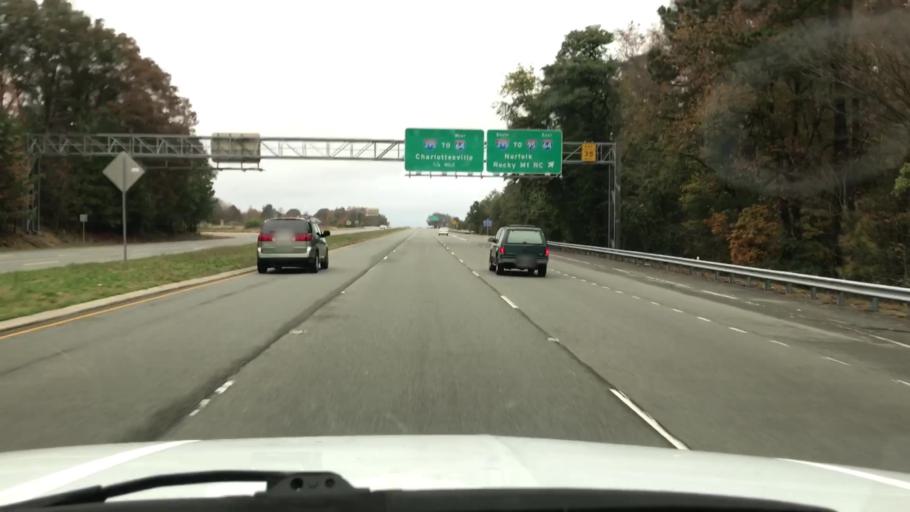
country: US
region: Virginia
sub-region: Henrico County
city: Chamberlayne
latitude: 37.6543
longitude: -77.4598
